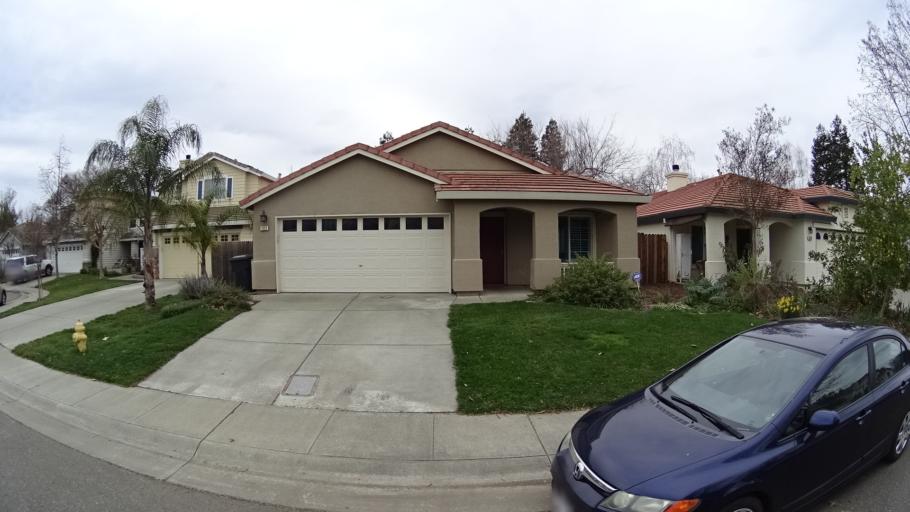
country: US
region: California
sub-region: Yolo County
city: Davis
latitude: 38.5586
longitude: -121.7001
